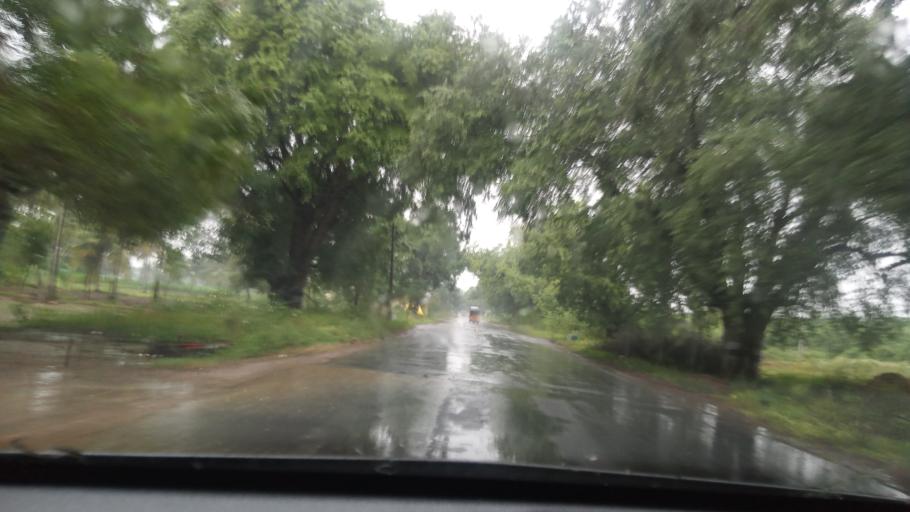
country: IN
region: Tamil Nadu
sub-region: Vellore
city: Walajapet
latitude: 12.8567
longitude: 79.3813
